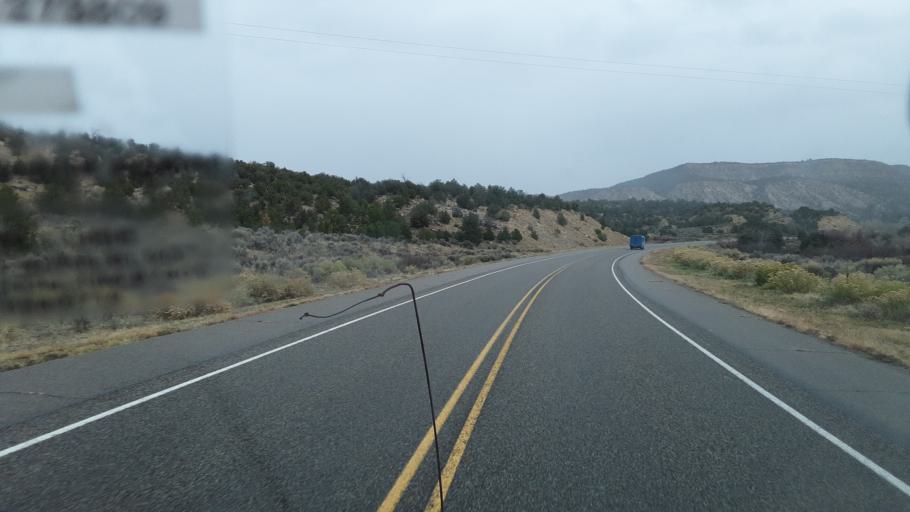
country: US
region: New Mexico
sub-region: Rio Arriba County
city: Santa Teresa
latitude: 36.3850
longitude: -106.5024
